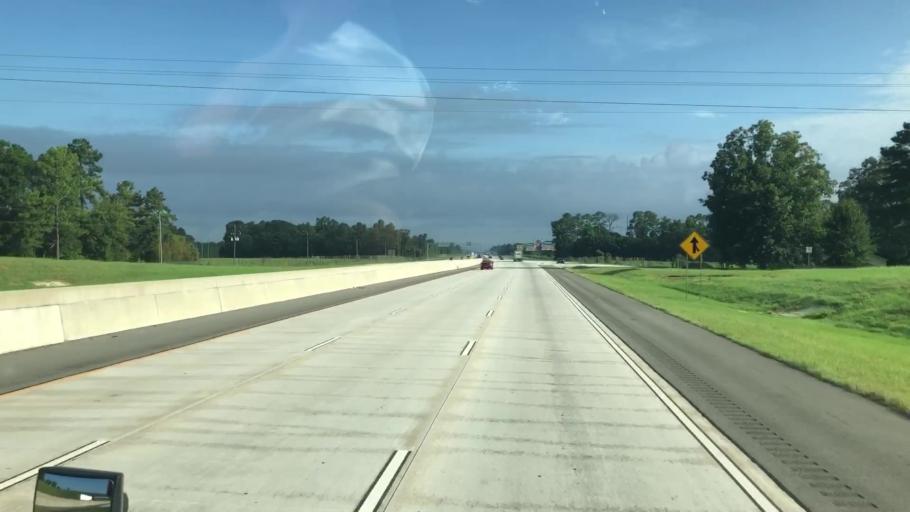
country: US
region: Georgia
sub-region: Cook County
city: Sparks
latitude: 31.2156
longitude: -83.4599
